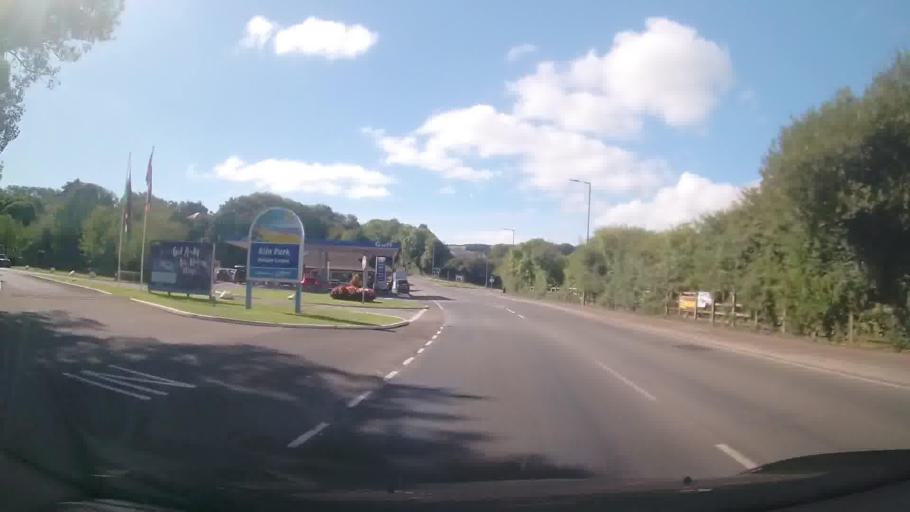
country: GB
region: Wales
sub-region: Pembrokeshire
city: Penally
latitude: 51.6694
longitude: -4.7236
